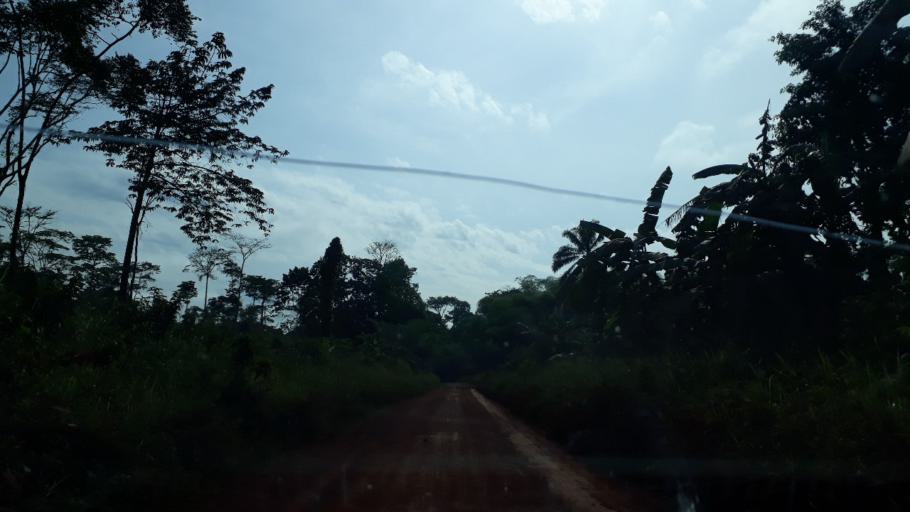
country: CD
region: Eastern Province
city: Wamba
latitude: 1.4170
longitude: 27.7822
